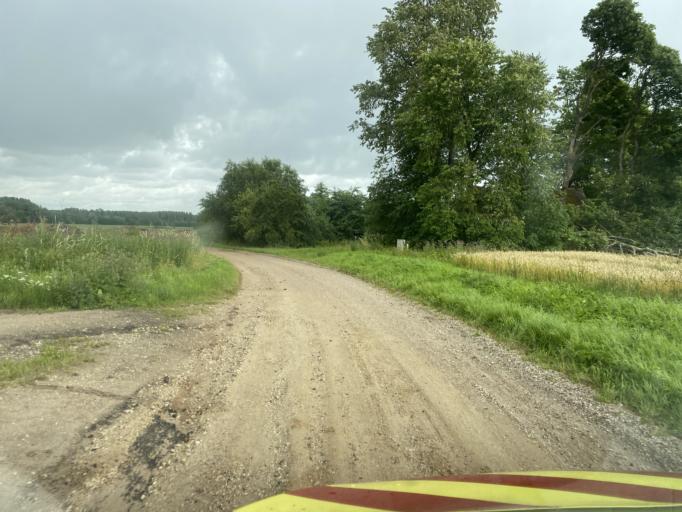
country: EE
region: Valgamaa
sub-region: Torva linn
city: Torva
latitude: 58.0921
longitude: 25.9054
